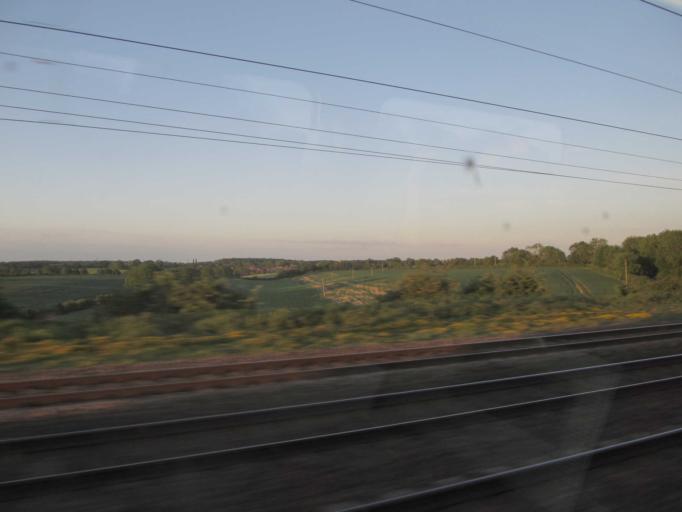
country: GB
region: England
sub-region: District of Rutland
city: Clipsham
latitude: 52.8095
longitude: -0.5405
